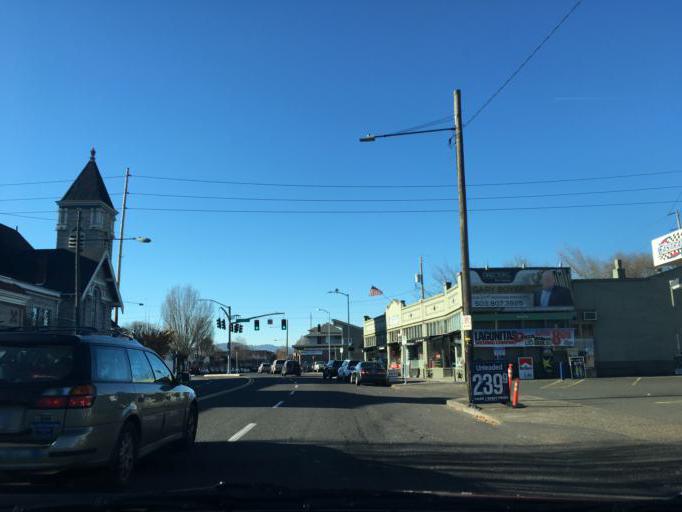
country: US
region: Oregon
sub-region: Multnomah County
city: Portland
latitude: 45.5353
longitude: -122.6400
